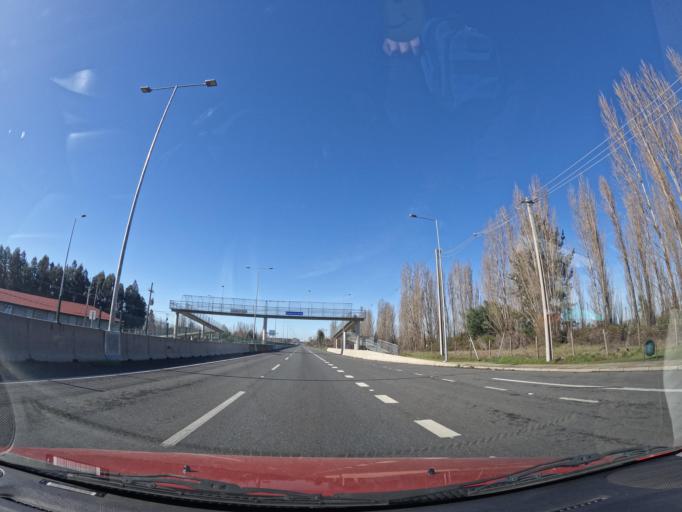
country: CL
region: Biobio
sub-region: Provincia de Biobio
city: Yumbel
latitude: -37.0036
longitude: -72.5396
